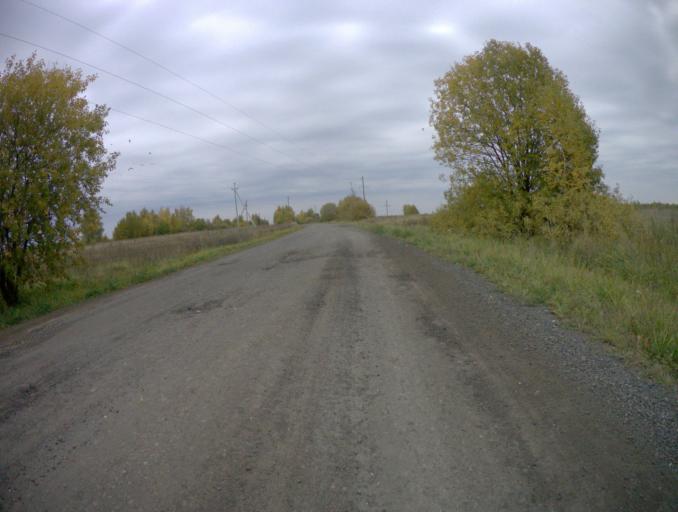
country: RU
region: Vladimir
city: Mstera
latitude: 56.3745
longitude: 41.8652
